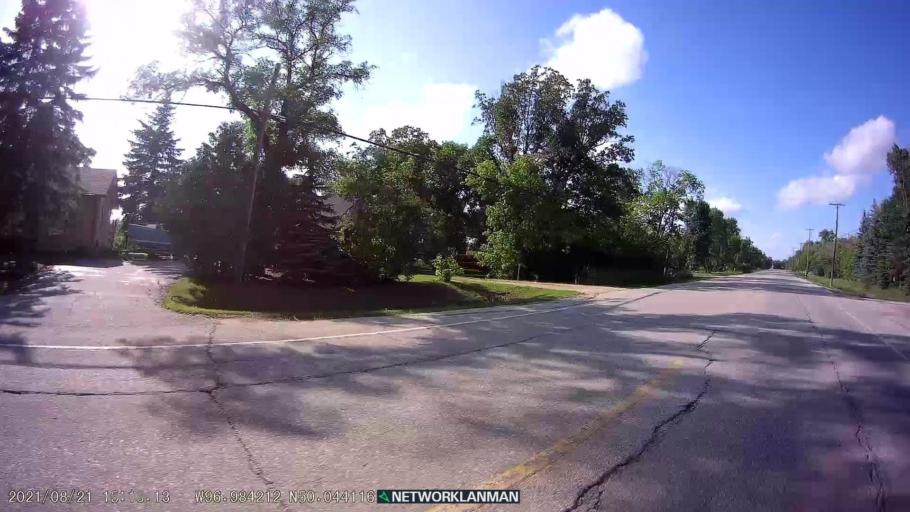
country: CA
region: Manitoba
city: Selkirk
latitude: 50.0445
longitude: -96.9841
